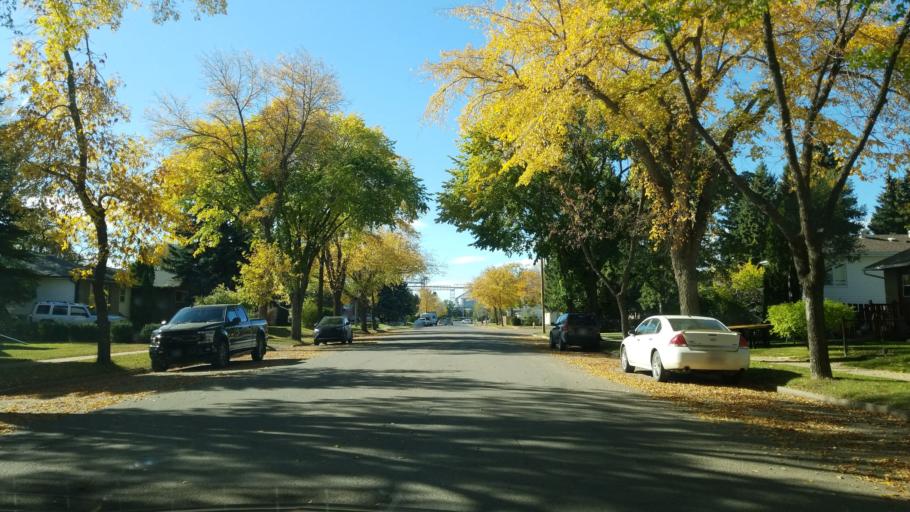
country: CA
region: Saskatchewan
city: Lloydminster
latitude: 53.2835
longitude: -110.0224
